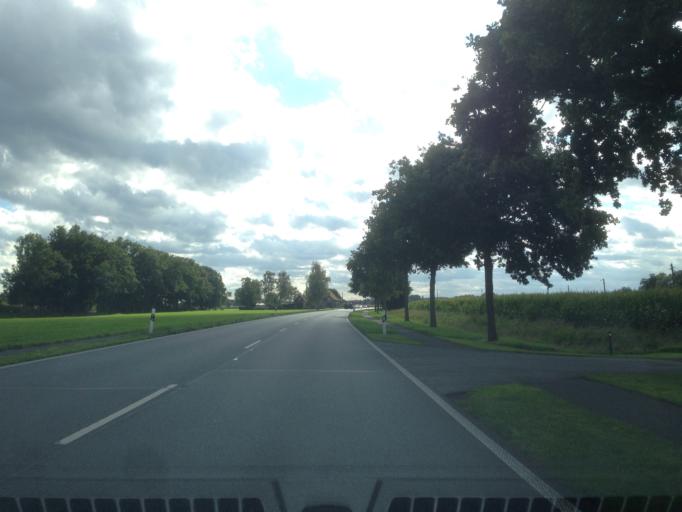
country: DE
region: North Rhine-Westphalia
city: Ludinghausen
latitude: 51.7924
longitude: 7.4685
